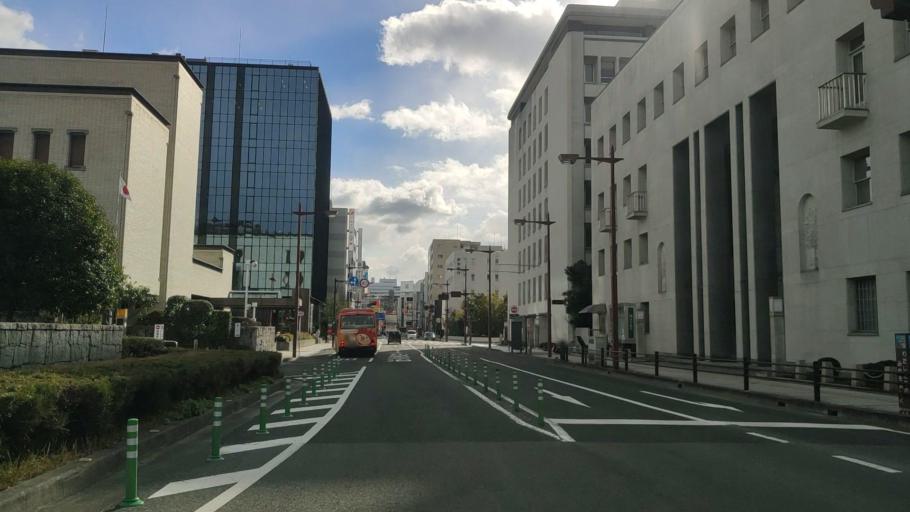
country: JP
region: Ehime
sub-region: Shikoku-chuo Shi
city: Matsuyama
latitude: 33.8392
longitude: 132.7648
